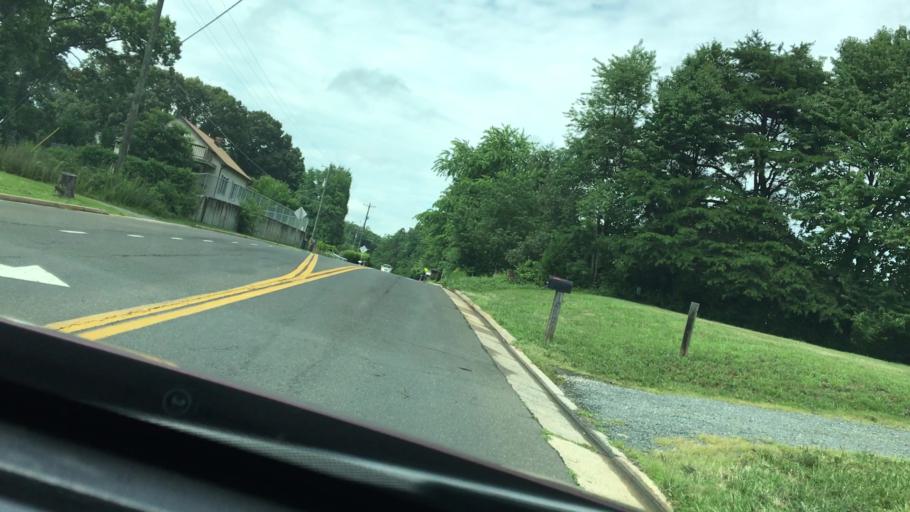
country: US
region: Virginia
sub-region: Prince William County
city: Buckhall
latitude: 38.7348
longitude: -77.4336
